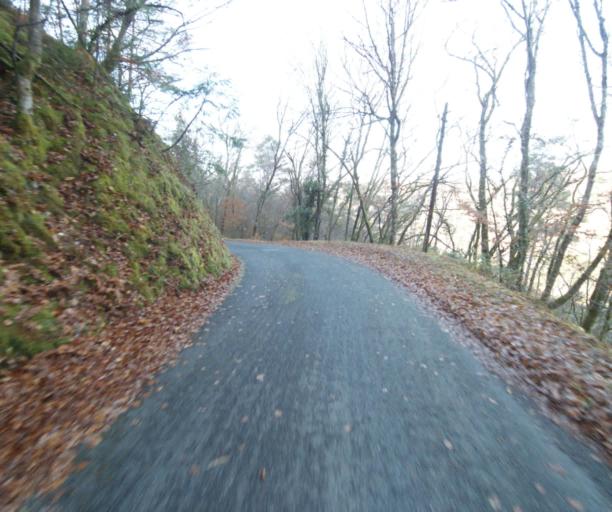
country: FR
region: Limousin
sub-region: Departement de la Correze
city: Laguenne
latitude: 45.2454
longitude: 1.7845
